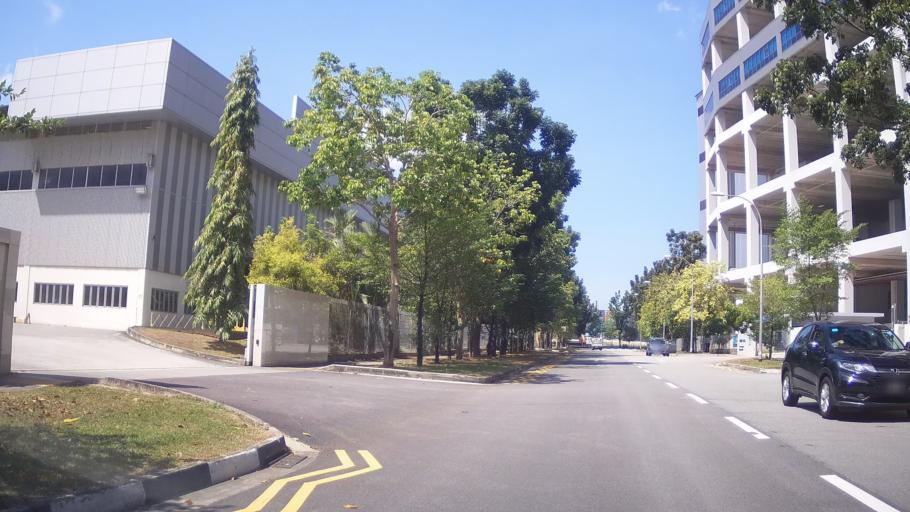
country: SG
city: Singapore
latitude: 1.3121
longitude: 103.6948
